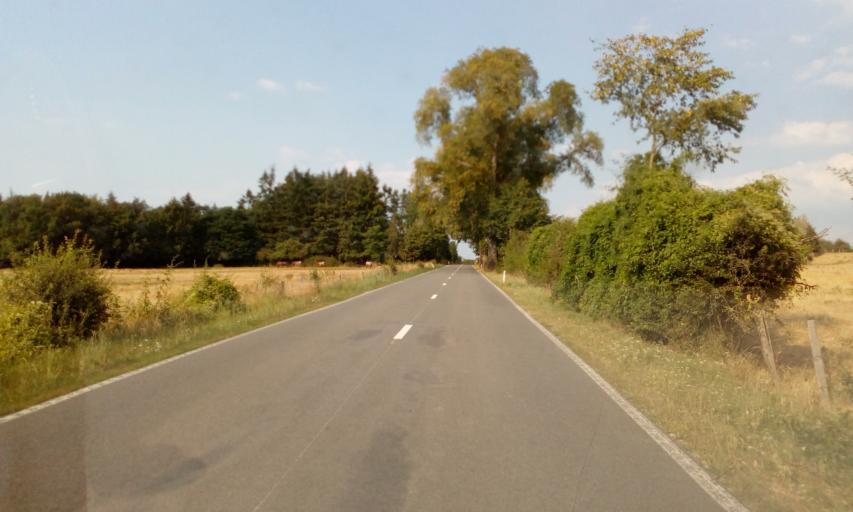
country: BE
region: Wallonia
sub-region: Province du Luxembourg
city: Tellin
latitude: 50.1124
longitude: 5.2411
